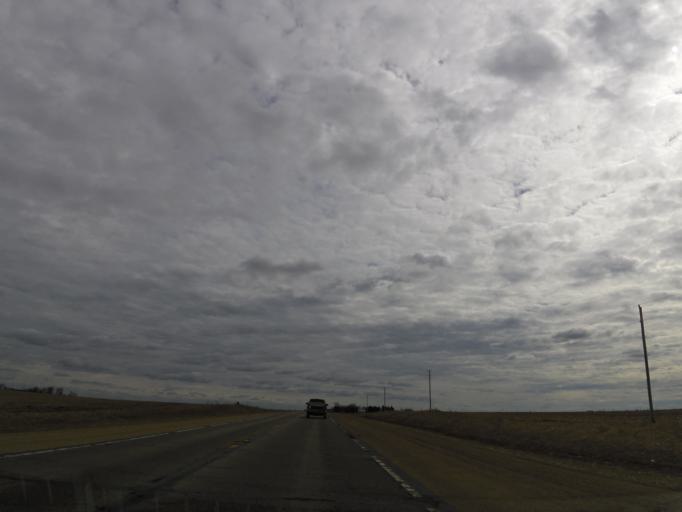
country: US
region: Iowa
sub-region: Howard County
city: Cresco
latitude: 43.3621
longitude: -92.2985
